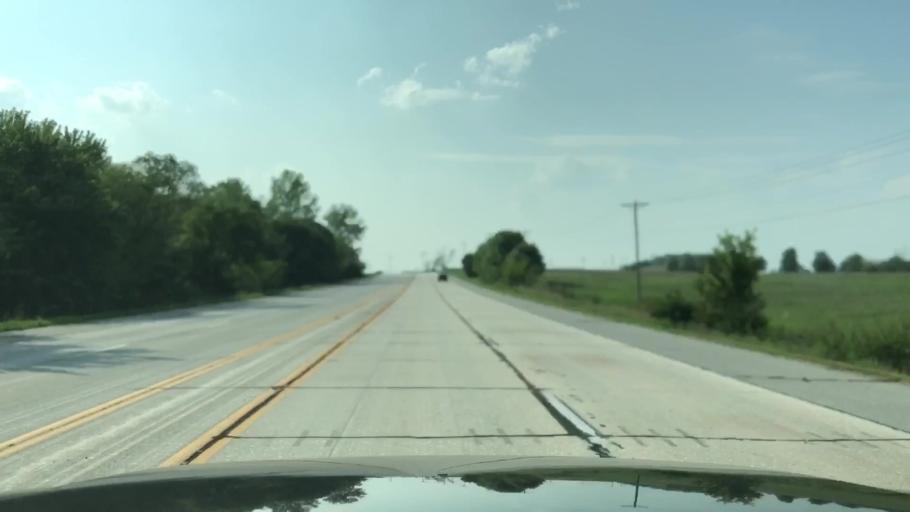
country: US
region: Missouri
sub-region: Saint Charles County
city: Wentzville
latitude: 38.8258
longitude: -90.8266
